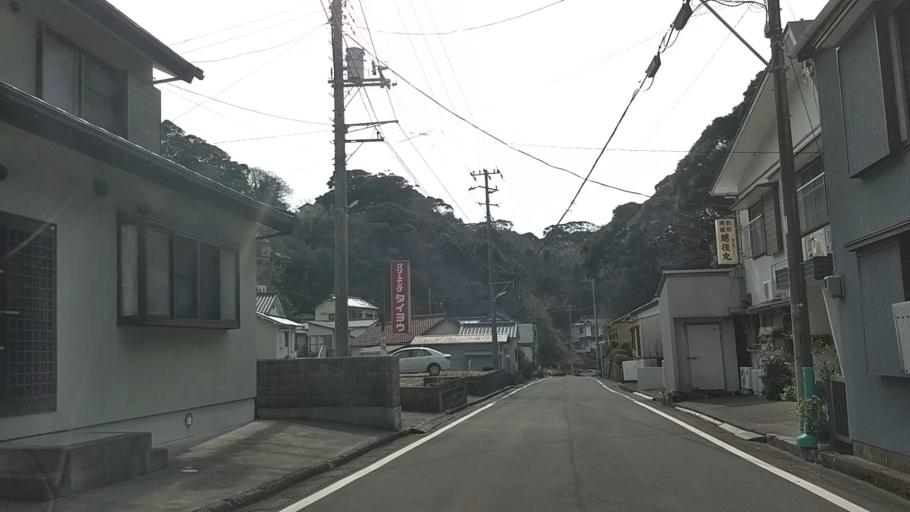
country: JP
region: Shizuoka
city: Shimoda
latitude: 34.6611
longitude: 138.9651
